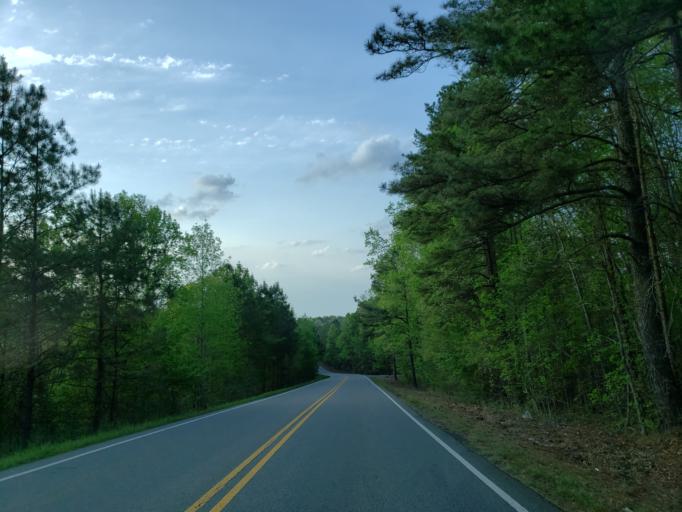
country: US
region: Georgia
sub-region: Cherokee County
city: Ball Ground
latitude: 34.2718
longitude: -84.3713
